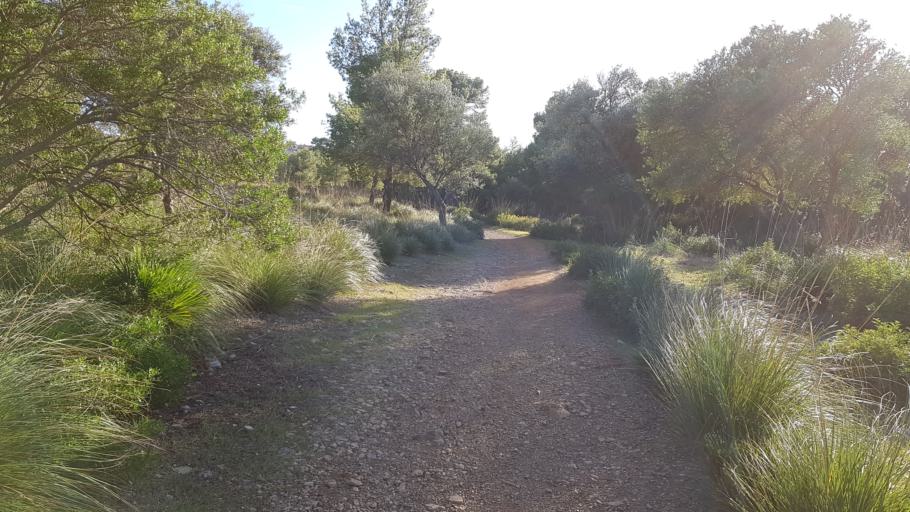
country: ES
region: Balearic Islands
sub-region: Illes Balears
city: Port d'Alcudia
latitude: 39.8657
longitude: 3.1580
